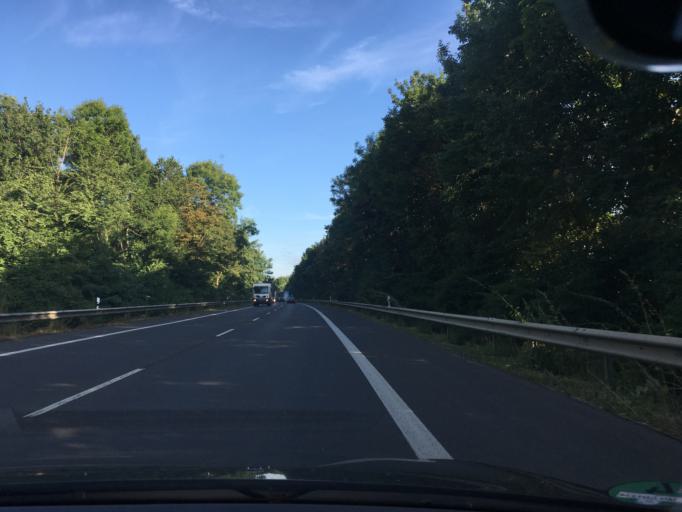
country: DE
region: North Rhine-Westphalia
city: Julich
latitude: 50.9615
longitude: 6.3705
